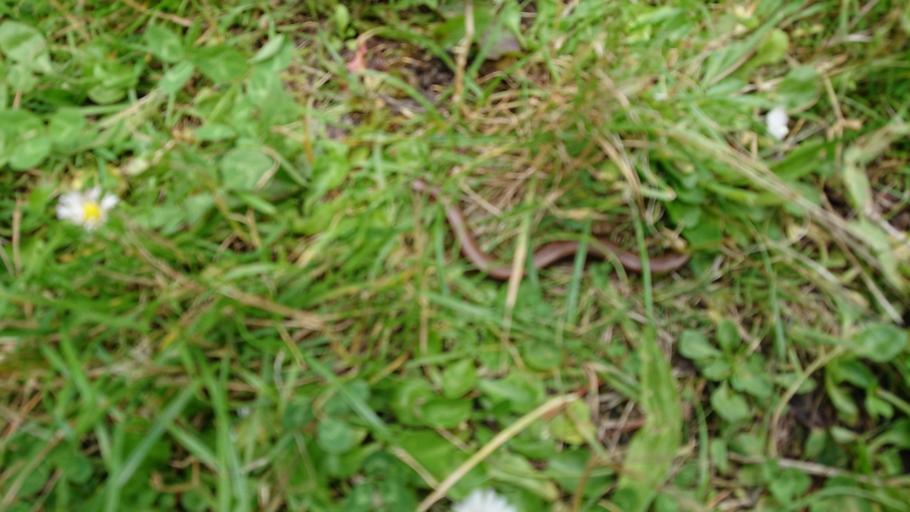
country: DK
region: North Denmark
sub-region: Hjorring Kommune
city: Sindal
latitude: 57.4454
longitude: 10.3452
